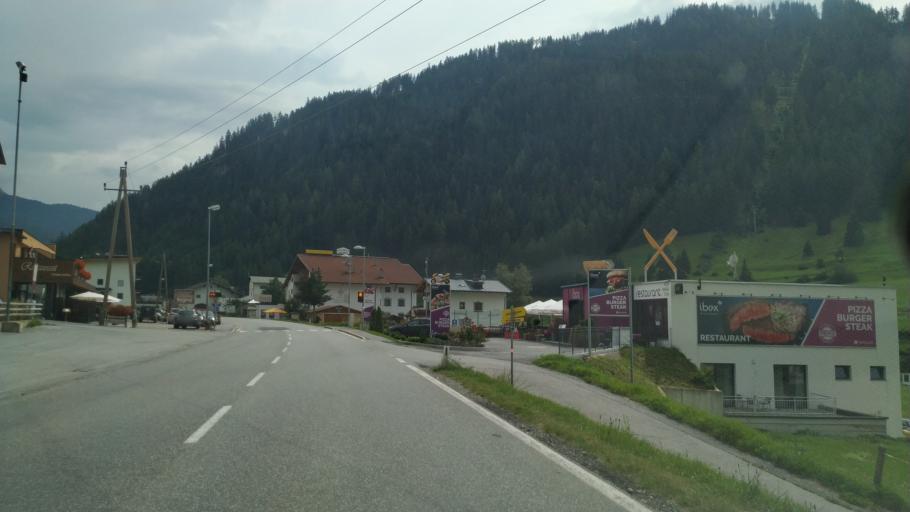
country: AT
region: Tyrol
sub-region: Politischer Bezirk Landeck
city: Nauders
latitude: 46.8919
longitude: 10.4986
